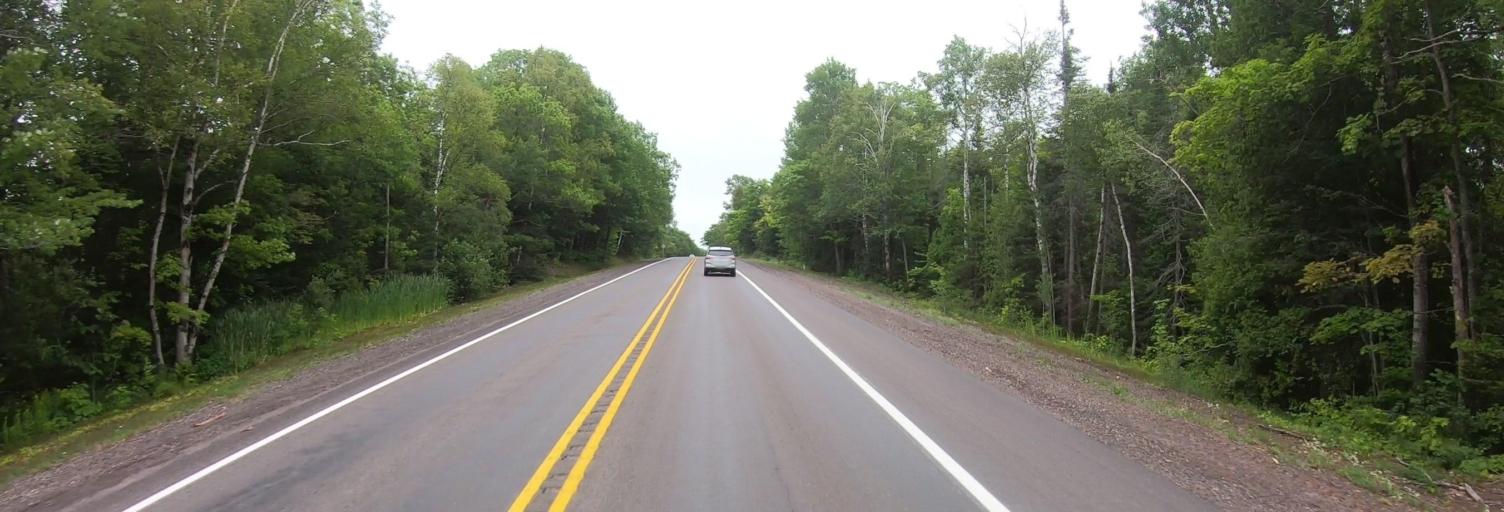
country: US
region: Michigan
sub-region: Keweenaw County
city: Eagle River
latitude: 47.3657
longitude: -88.3065
